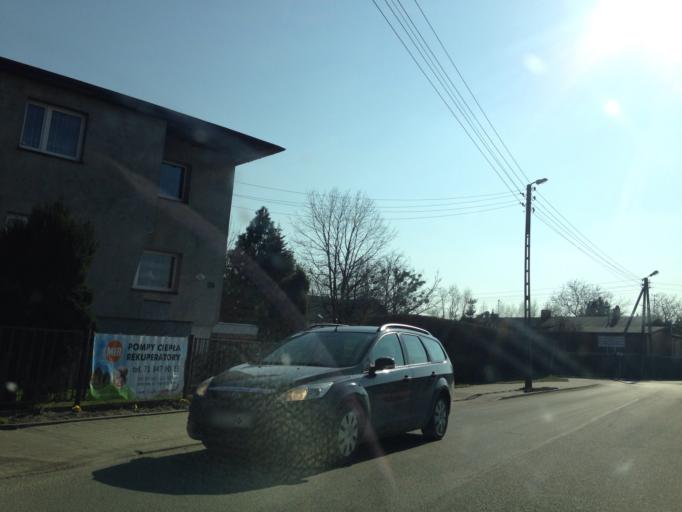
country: PL
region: Lower Silesian Voivodeship
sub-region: Powiat wroclawski
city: Dlugoleka
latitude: 51.1796
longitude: 17.2009
